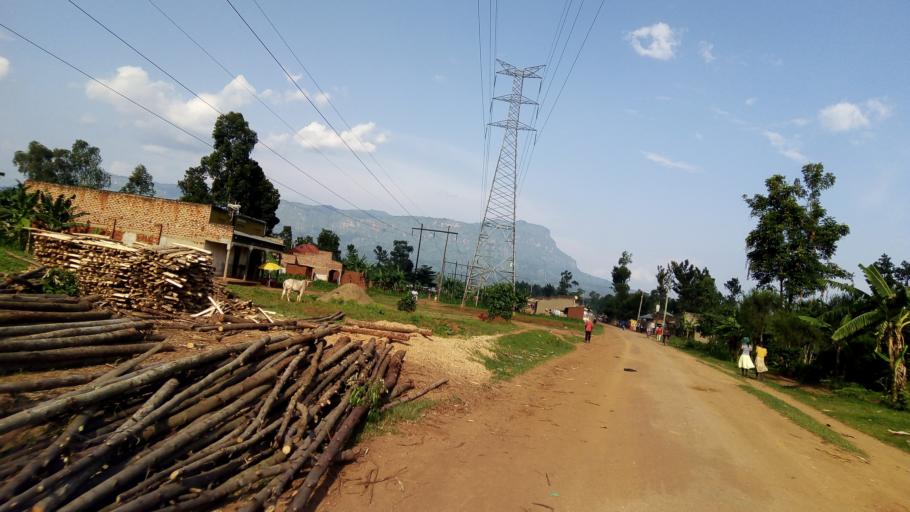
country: UG
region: Eastern Region
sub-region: Mbale District
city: Mbale
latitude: 1.0576
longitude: 34.1585
